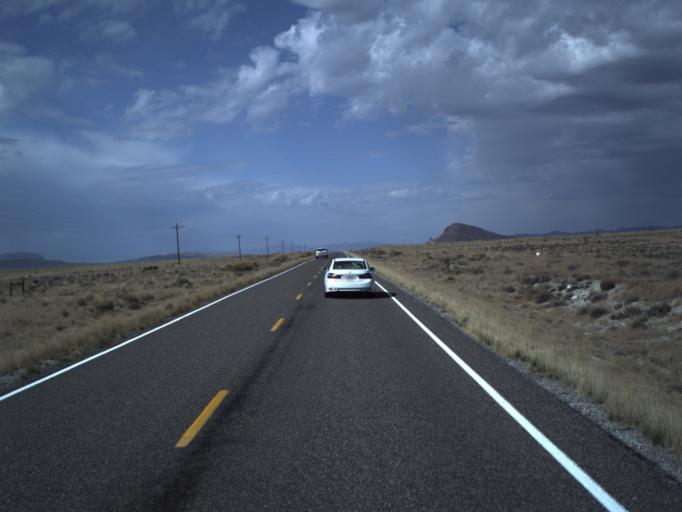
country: US
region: Utah
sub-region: Tooele County
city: Wendover
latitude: 41.4360
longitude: -113.7511
